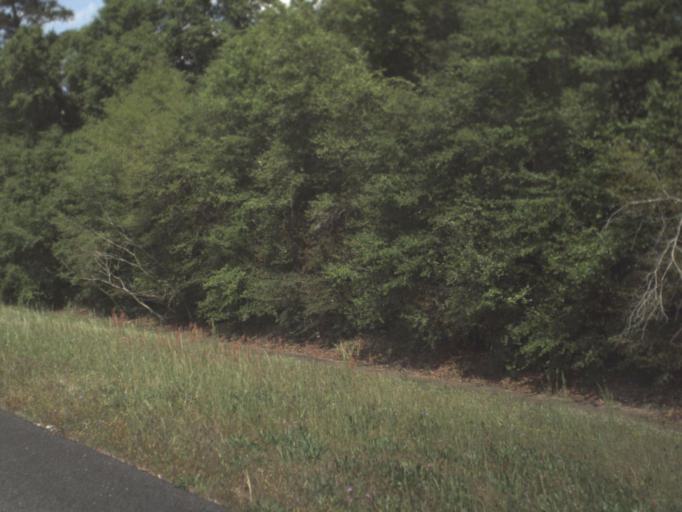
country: US
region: Florida
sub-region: Escambia County
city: Century
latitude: 30.9148
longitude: -87.3151
